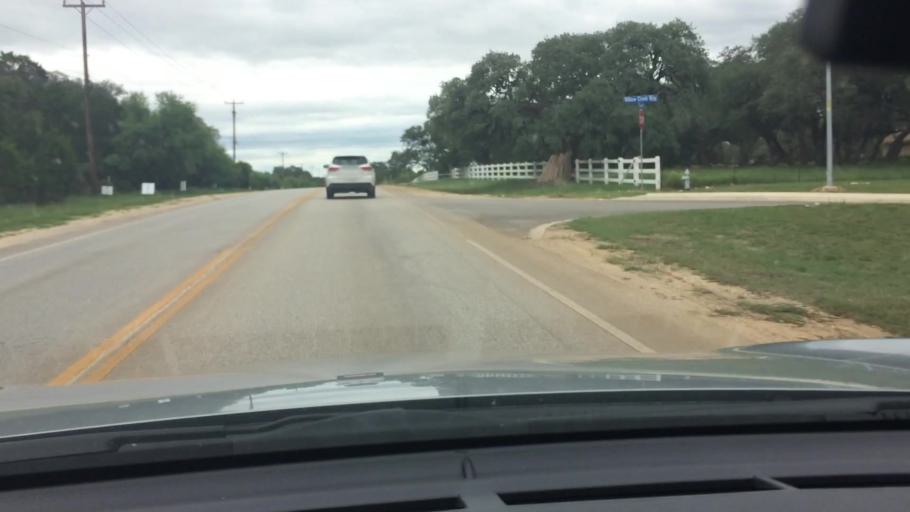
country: US
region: Texas
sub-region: Comal County
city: Garden Ridge
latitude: 29.6359
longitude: -98.3759
